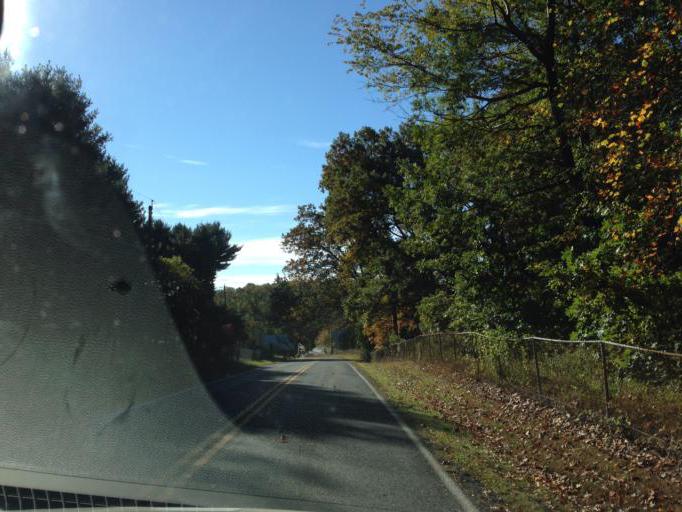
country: US
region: Maryland
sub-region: Howard County
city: Fulton
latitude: 39.1417
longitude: -76.9177
